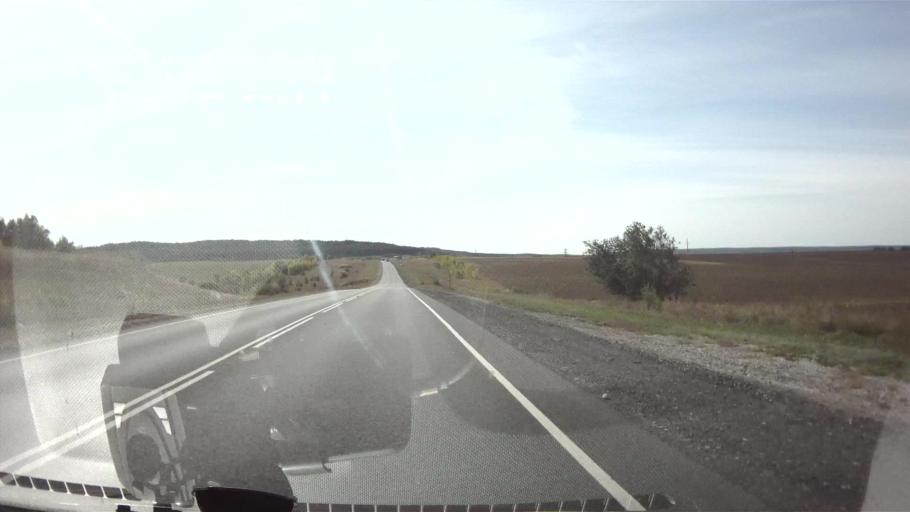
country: RU
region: Saratov
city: Khvalynsk
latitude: 52.5554
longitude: 48.0811
